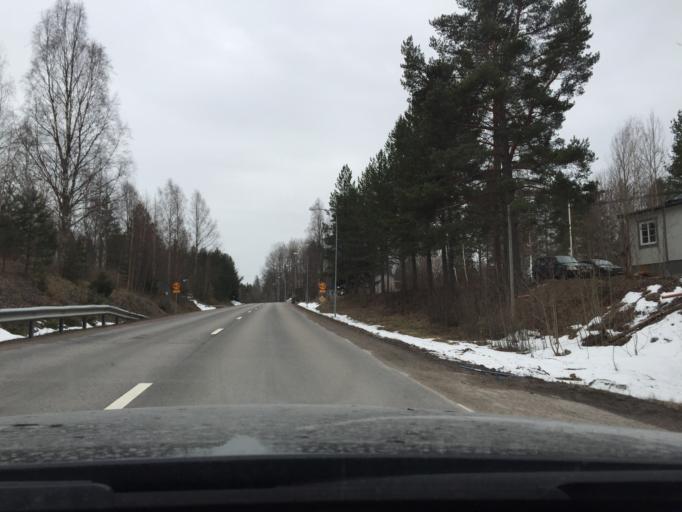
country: SE
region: Gaevleborg
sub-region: Sandvikens Kommun
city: Jarbo
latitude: 60.7577
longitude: 16.5352
